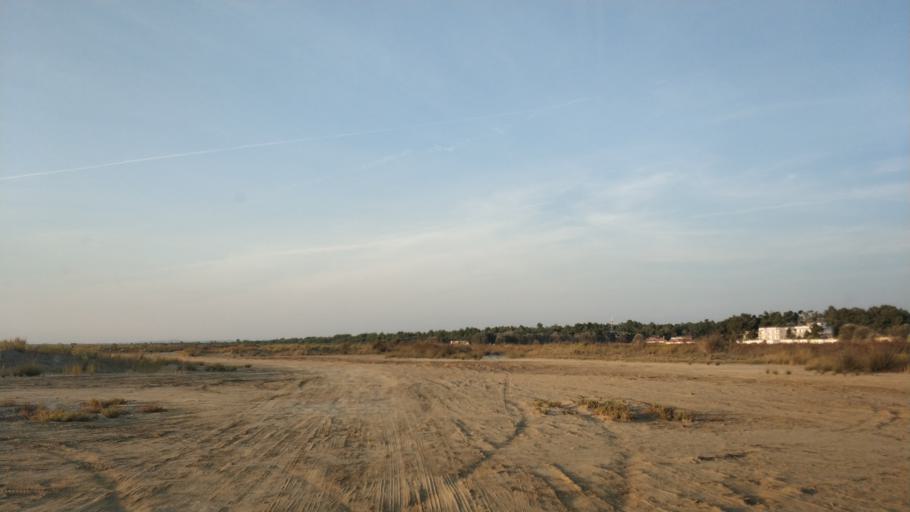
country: AL
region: Fier
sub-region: Rrethi i Lushnjes
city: Divjake
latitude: 40.9678
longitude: 19.4758
